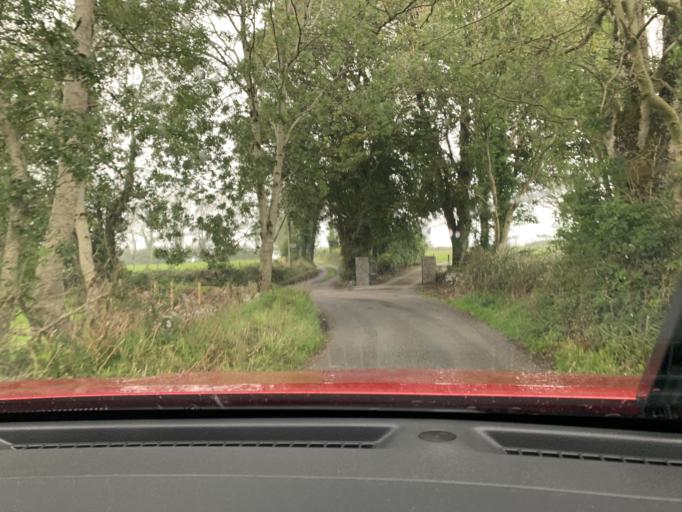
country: IE
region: Connaught
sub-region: County Leitrim
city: Carrick-on-Shannon
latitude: 53.8738
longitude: -8.1271
